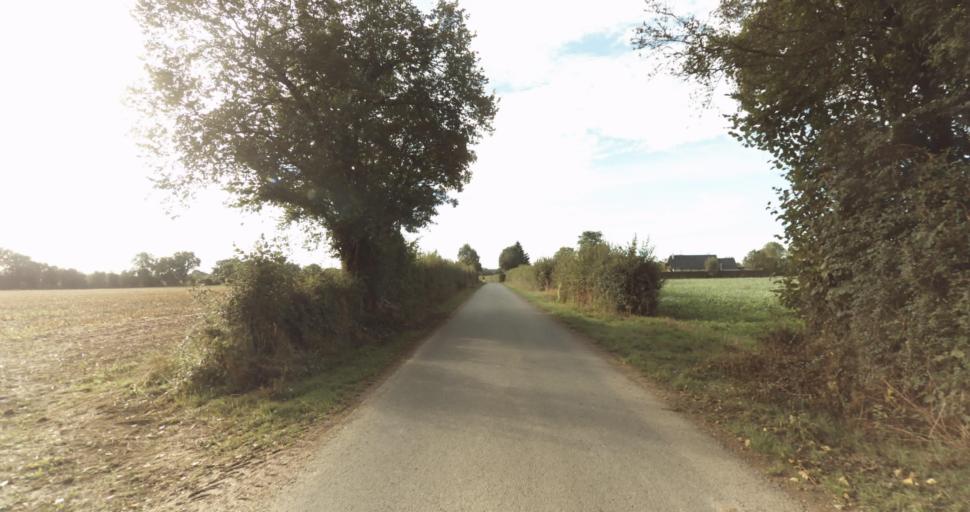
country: FR
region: Lower Normandy
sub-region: Departement de l'Orne
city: Vimoutiers
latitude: 48.8857
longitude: 0.2406
